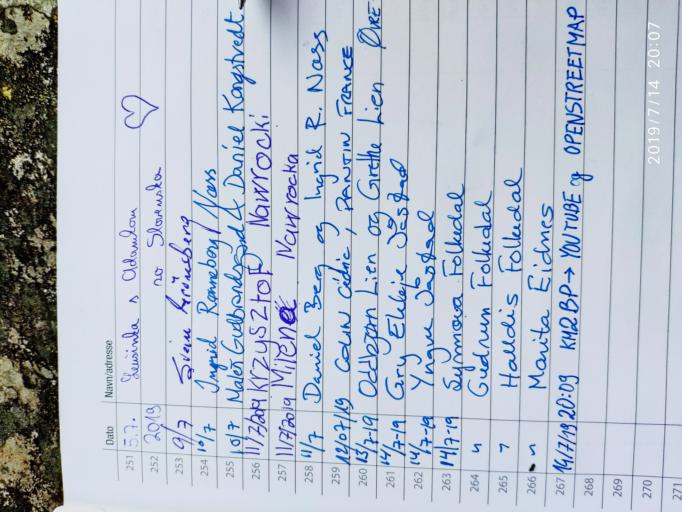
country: NO
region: Hordaland
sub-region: Ullensvang
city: Kinsarvik
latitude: 60.3131
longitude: 6.6654
